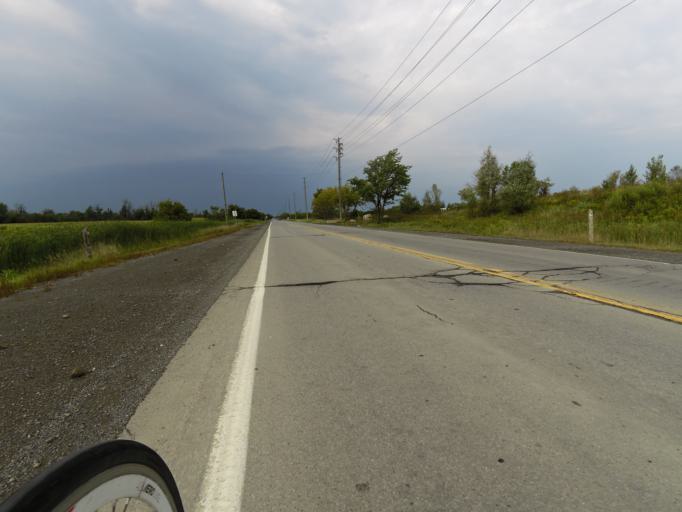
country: CA
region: Ontario
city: Bells Corners
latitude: 45.2467
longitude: -75.7617
